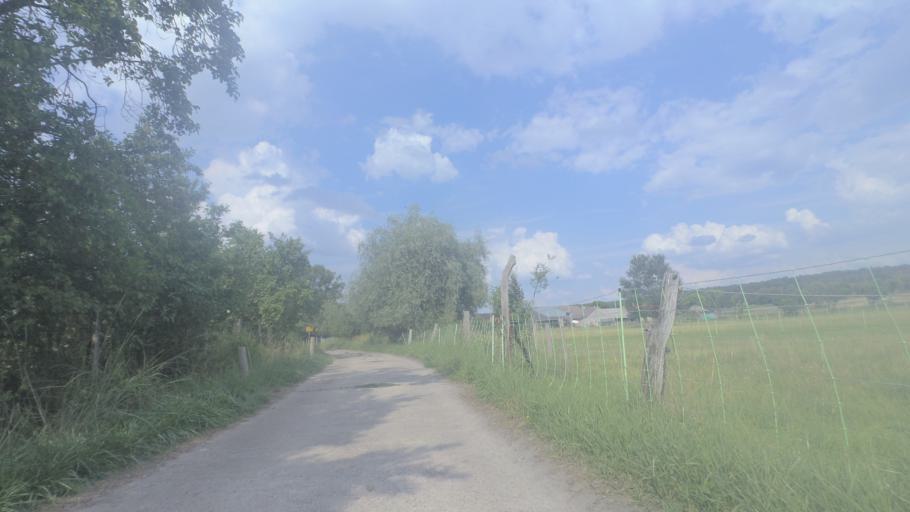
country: DE
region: Brandenburg
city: Michendorf
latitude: 52.2421
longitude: 13.0831
